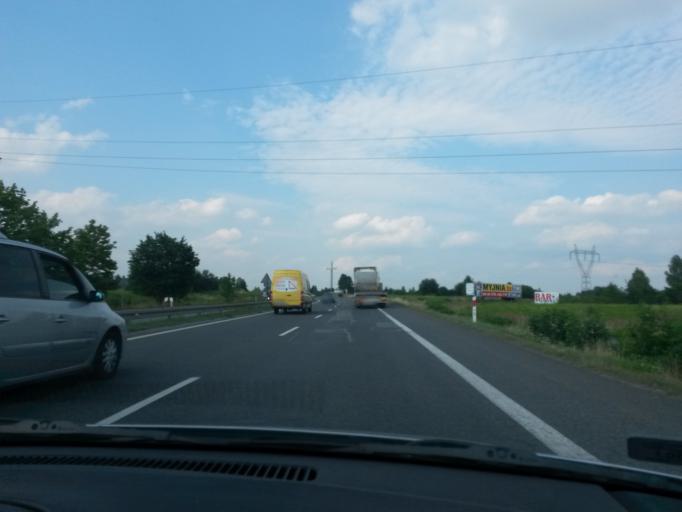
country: PL
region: Silesian Voivodeship
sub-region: Dabrowa Gornicza
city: Dabrowa Gornicza
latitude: 50.2814
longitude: 19.2140
